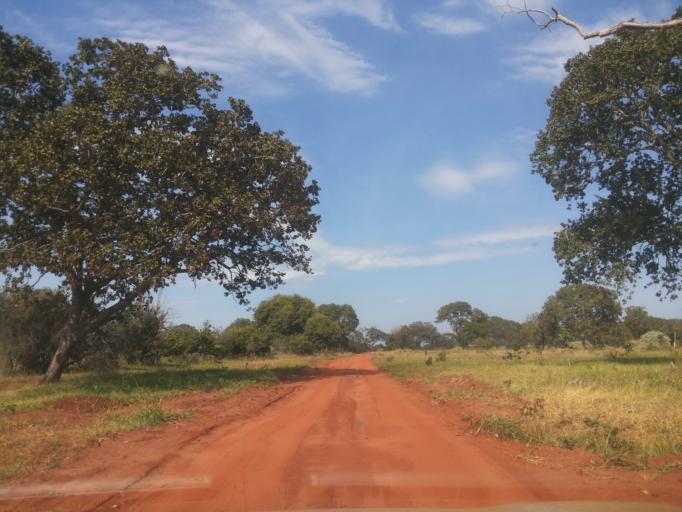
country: BR
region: Minas Gerais
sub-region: Ituiutaba
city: Ituiutaba
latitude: -19.0592
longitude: -49.3642
